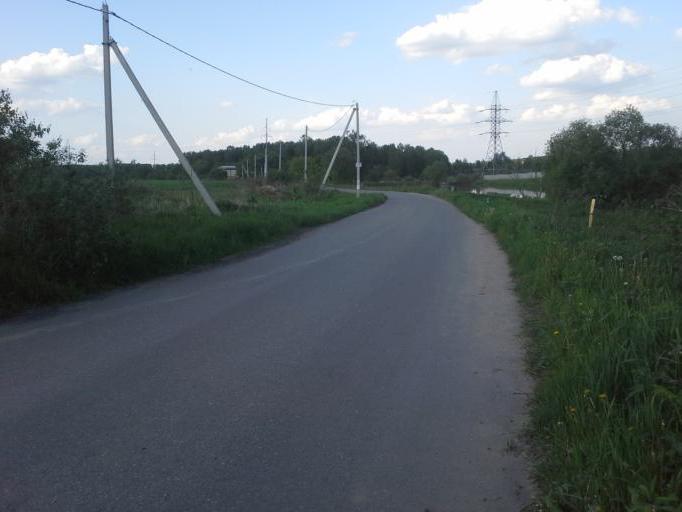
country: RU
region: Moskovskaya
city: Zhavoronki
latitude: 55.6579
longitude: 37.1341
